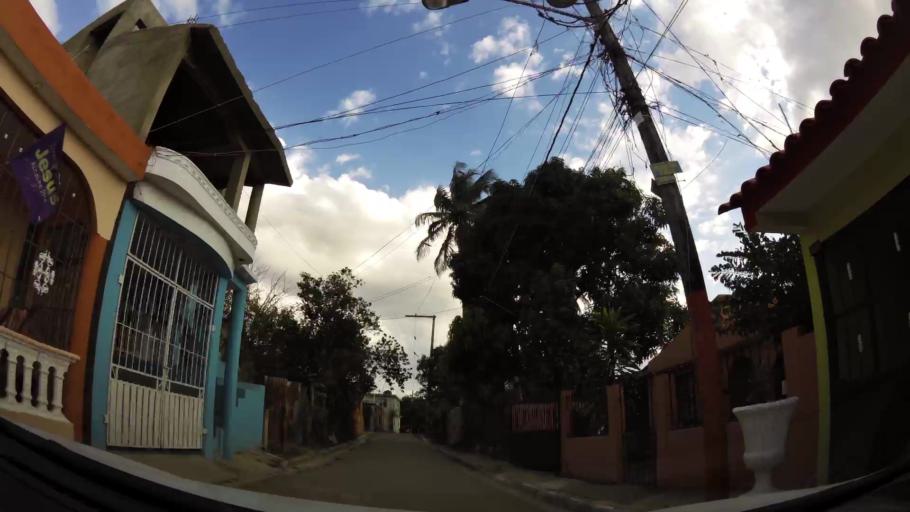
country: DO
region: Nacional
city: Ensanche Luperon
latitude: 18.5574
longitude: -69.9088
